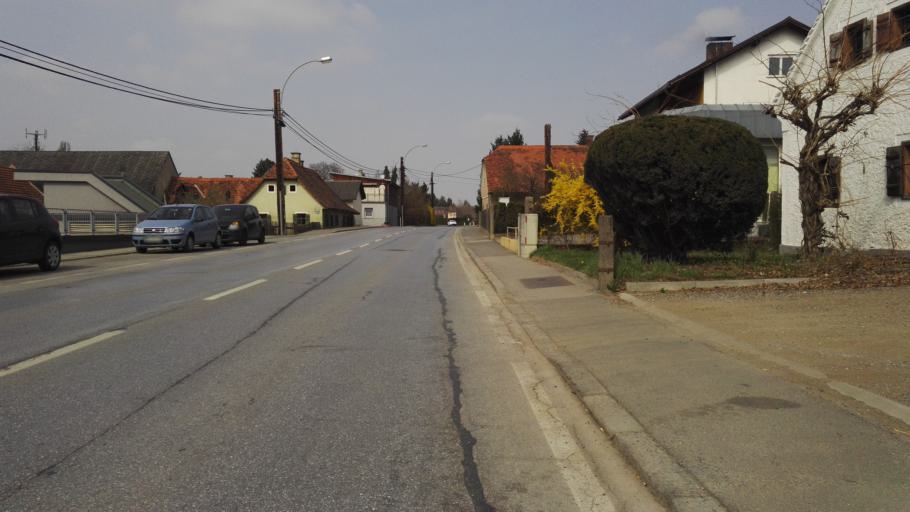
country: AT
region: Styria
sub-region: Politischer Bezirk Graz-Umgebung
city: Feldkirchen bei Graz
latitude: 47.0206
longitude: 15.4714
